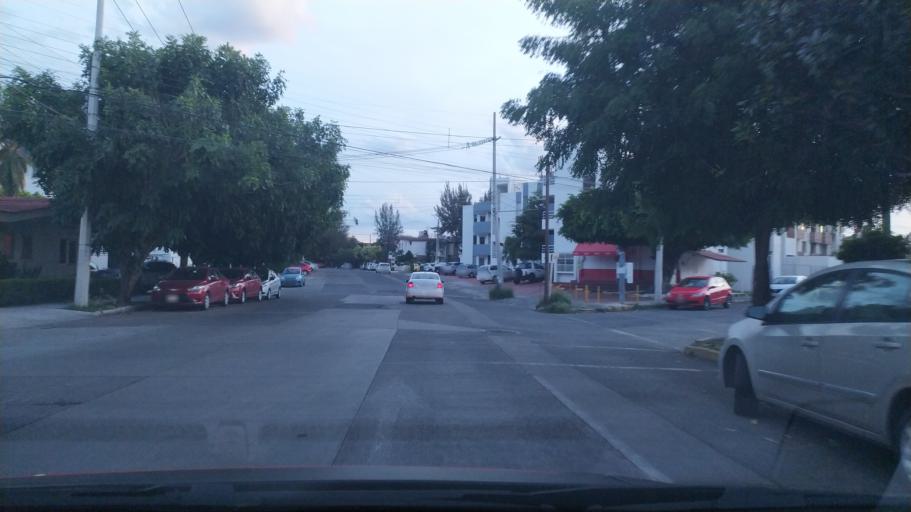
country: MX
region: Jalisco
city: Guadalajara
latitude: 20.6411
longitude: -103.4125
